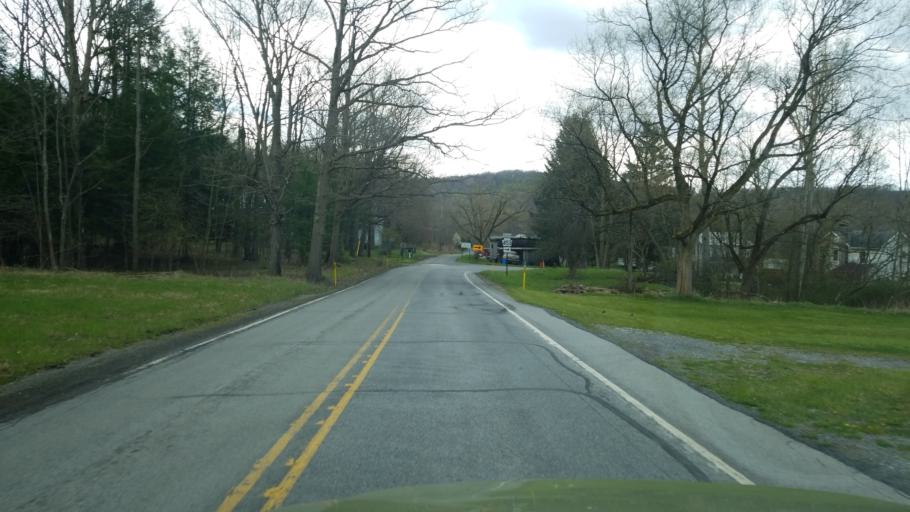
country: US
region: Pennsylvania
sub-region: Clearfield County
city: Curwensville
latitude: 40.8906
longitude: -78.4607
